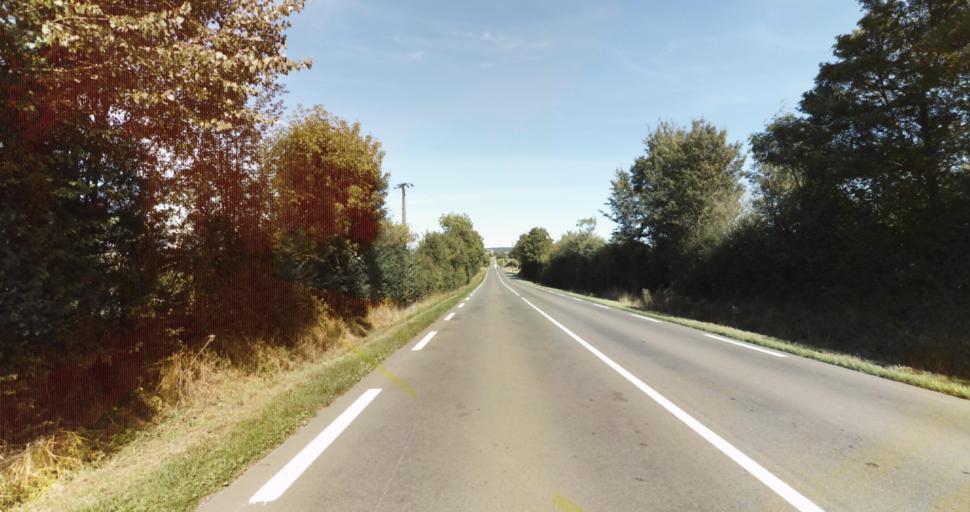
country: FR
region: Lower Normandy
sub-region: Departement de l'Orne
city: Gace
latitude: 48.7390
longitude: 0.2599
